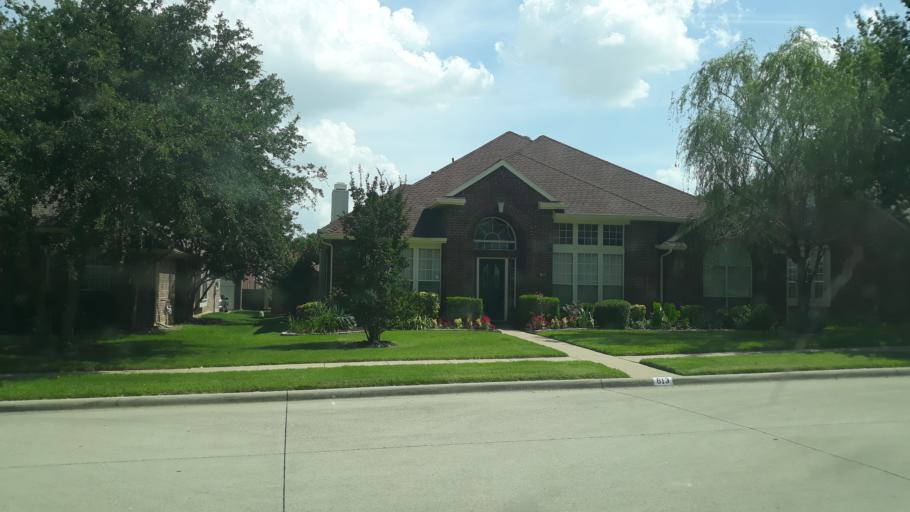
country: US
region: Texas
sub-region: Dallas County
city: Coppell
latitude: 32.9691
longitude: -97.0114
